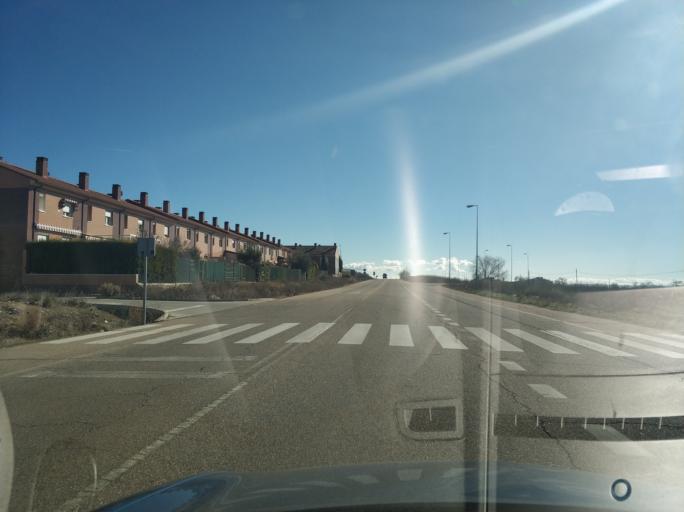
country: ES
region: Castille and Leon
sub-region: Provincia de Valladolid
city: Cisterniga
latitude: 41.6067
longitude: -4.6813
